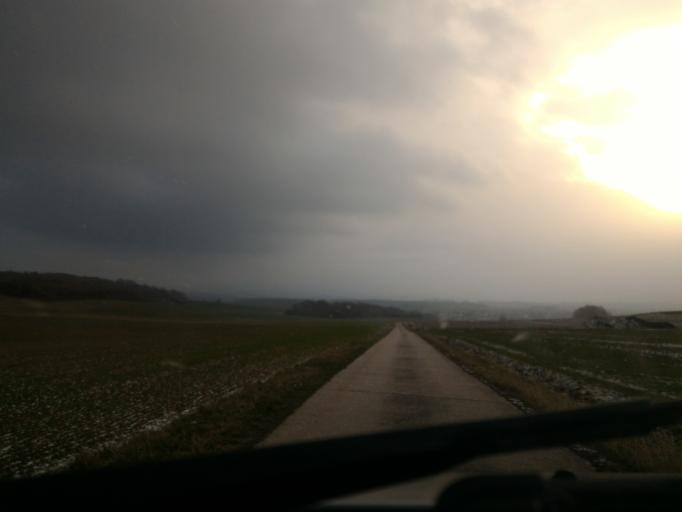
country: DE
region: Saxony
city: Bertsdorf-Hoernitz
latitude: 50.8961
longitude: 14.7145
